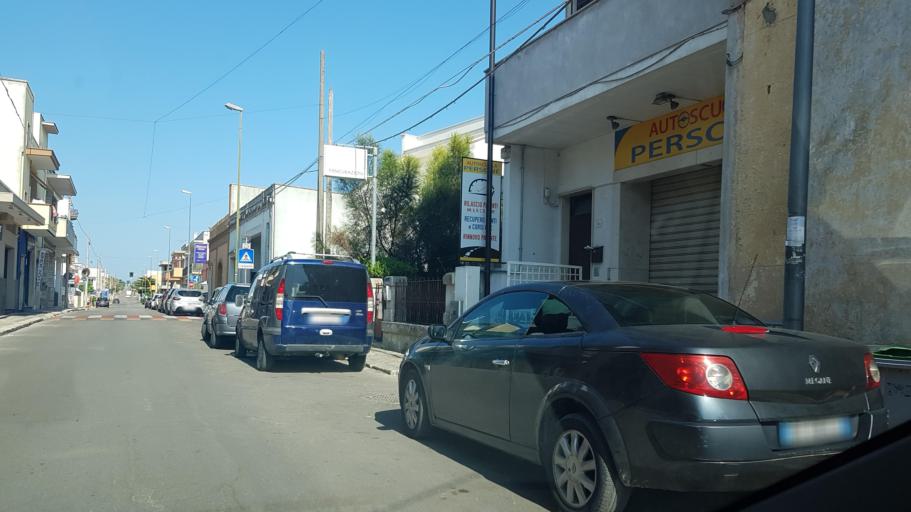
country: IT
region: Apulia
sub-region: Provincia di Lecce
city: Taurisano
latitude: 39.9581
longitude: 18.2171
